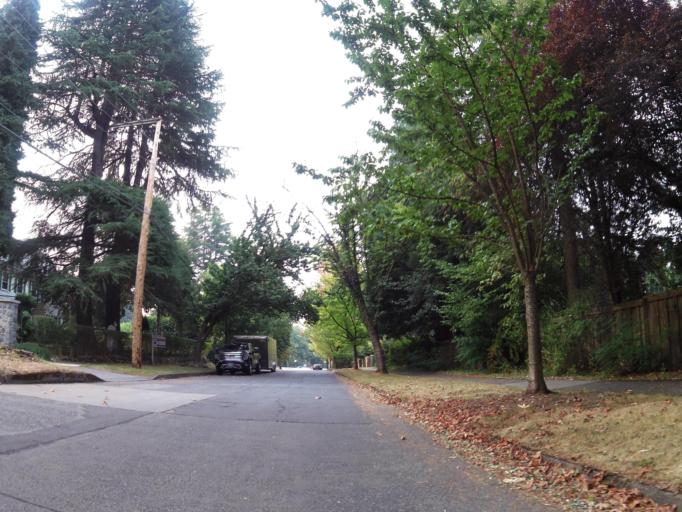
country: CA
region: British Columbia
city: Vancouver
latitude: 49.2510
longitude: -123.1488
